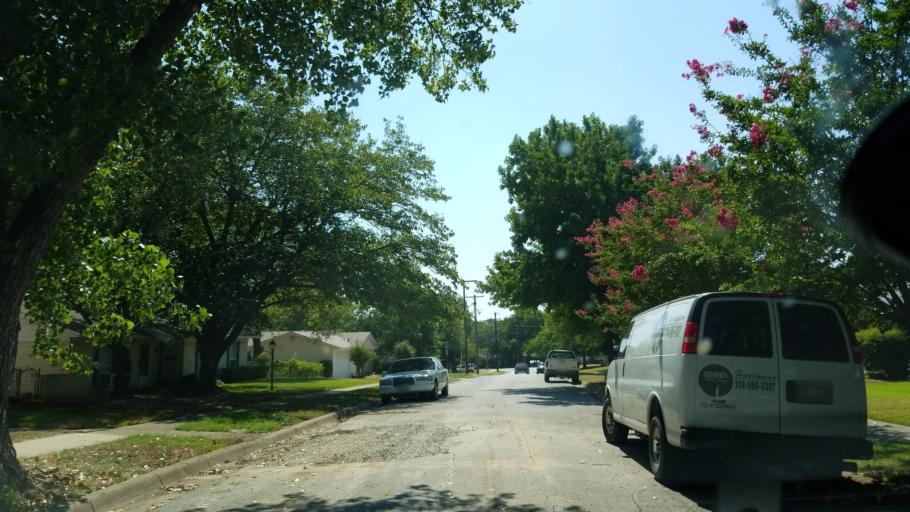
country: US
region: Texas
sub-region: Dallas County
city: Duncanville
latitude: 32.6560
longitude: -96.9037
